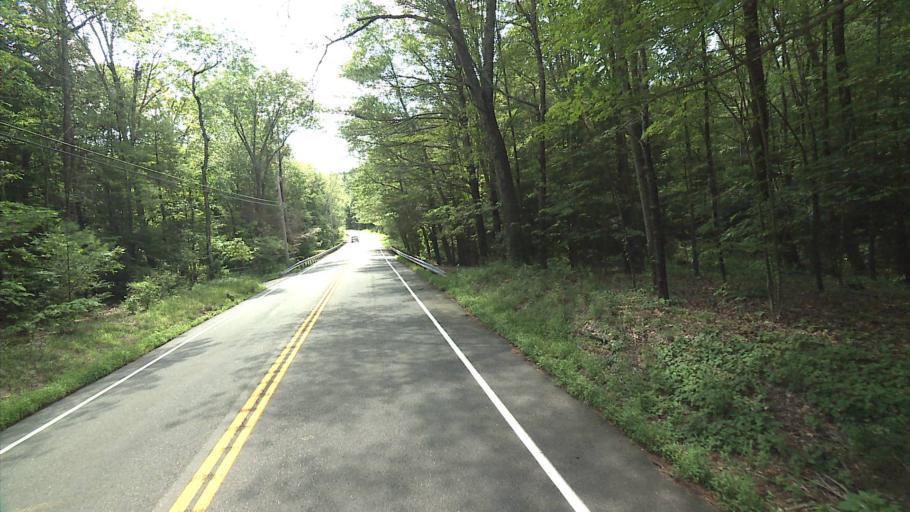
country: US
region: Massachusetts
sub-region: Worcester County
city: Southbridge
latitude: 41.9949
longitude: -72.0835
